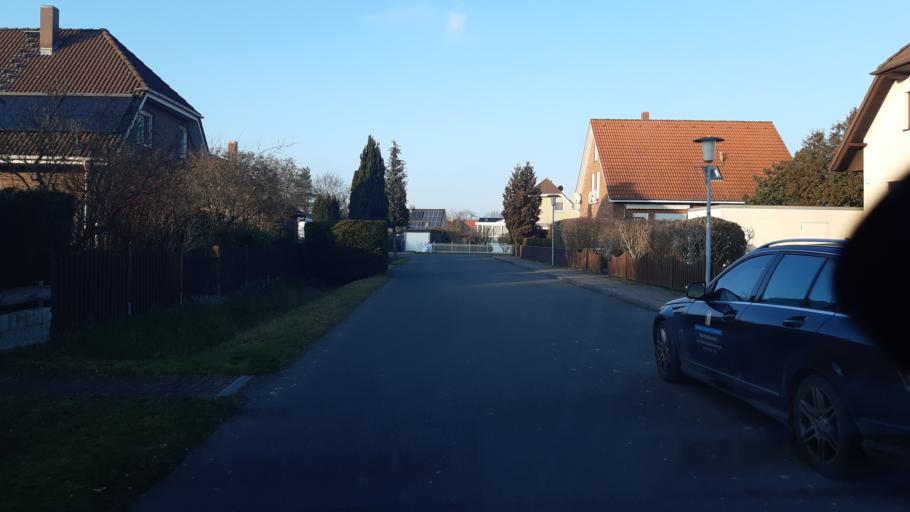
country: DE
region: Brandenburg
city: Velten
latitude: 52.7145
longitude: 13.1511
